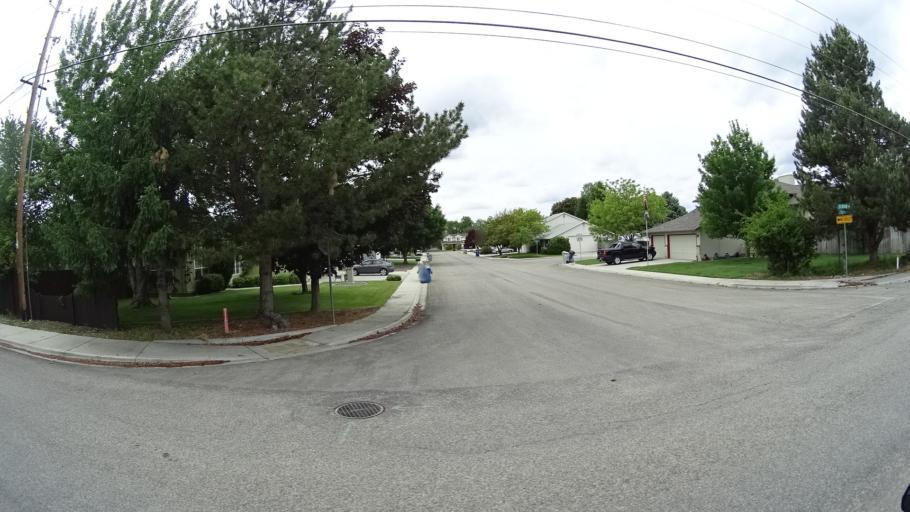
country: US
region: Idaho
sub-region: Ada County
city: Eagle
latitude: 43.6923
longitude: -116.3340
